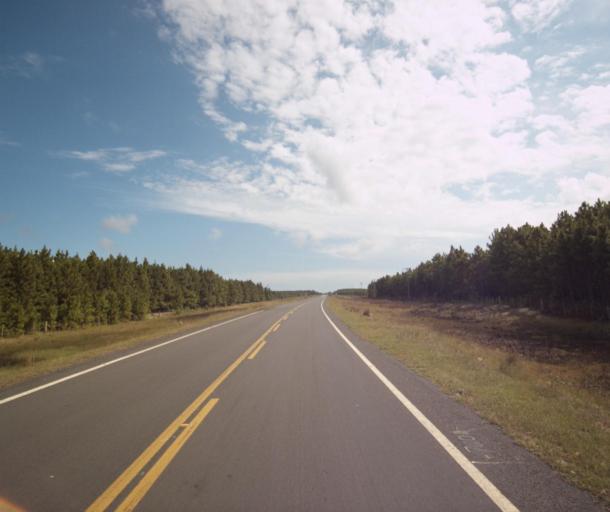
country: BR
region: Rio Grande do Sul
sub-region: Sao Lourenco Do Sul
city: Sao Lourenco do Sul
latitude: -31.5922
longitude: -51.3704
